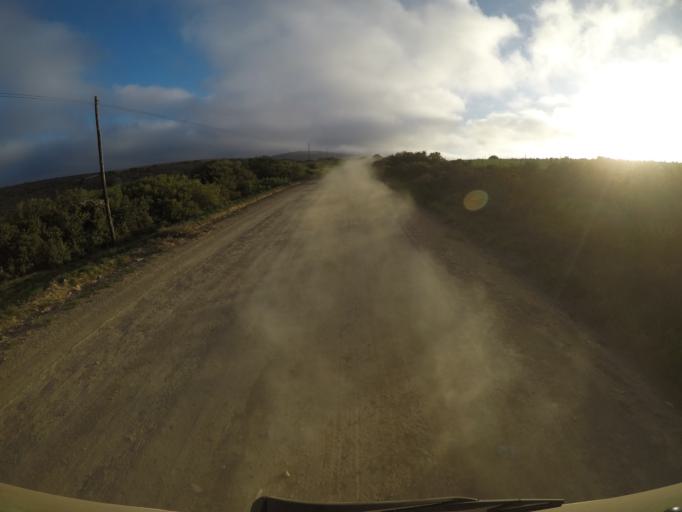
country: ZA
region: Western Cape
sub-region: Eden District Municipality
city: Mossel Bay
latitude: -34.1317
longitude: 22.0460
